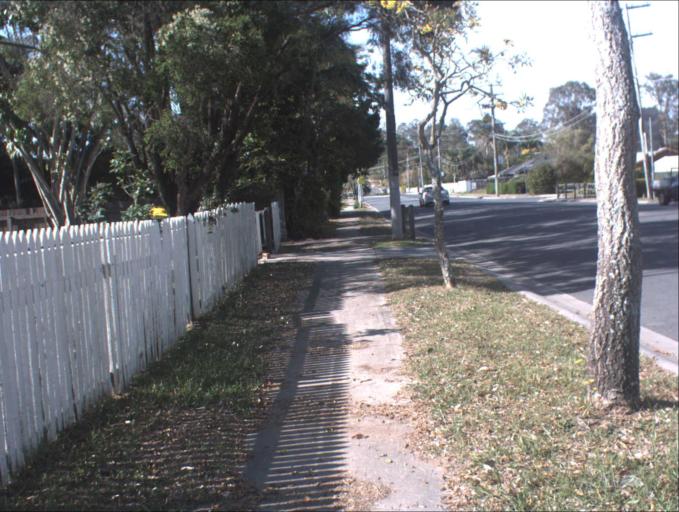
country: AU
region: Queensland
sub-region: Logan
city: Beenleigh
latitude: -27.6837
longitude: 153.1797
